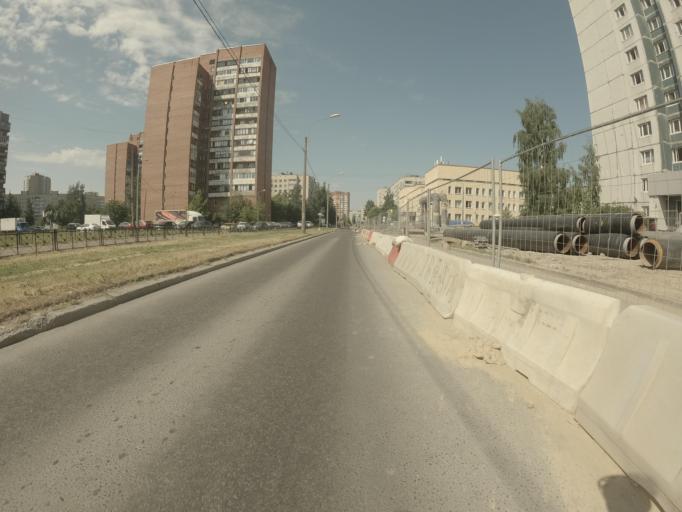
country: RU
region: St.-Petersburg
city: Krasnogvargeisky
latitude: 59.9409
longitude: 30.4838
